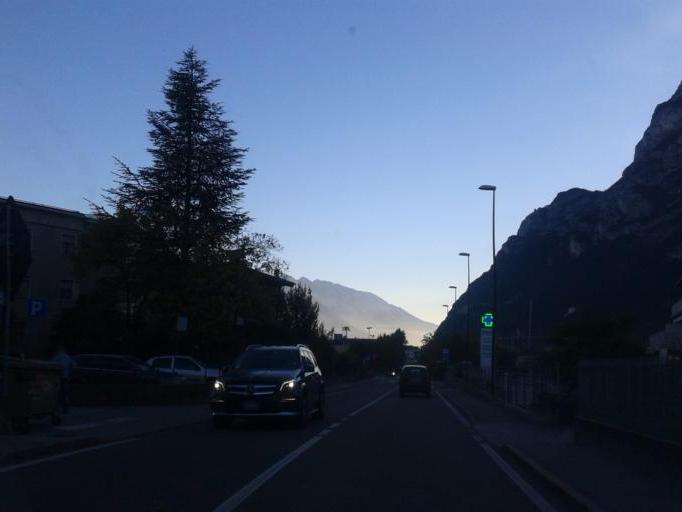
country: IT
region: Trentino-Alto Adige
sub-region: Provincia di Trento
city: Riva del Garda
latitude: 45.9003
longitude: 10.8446
